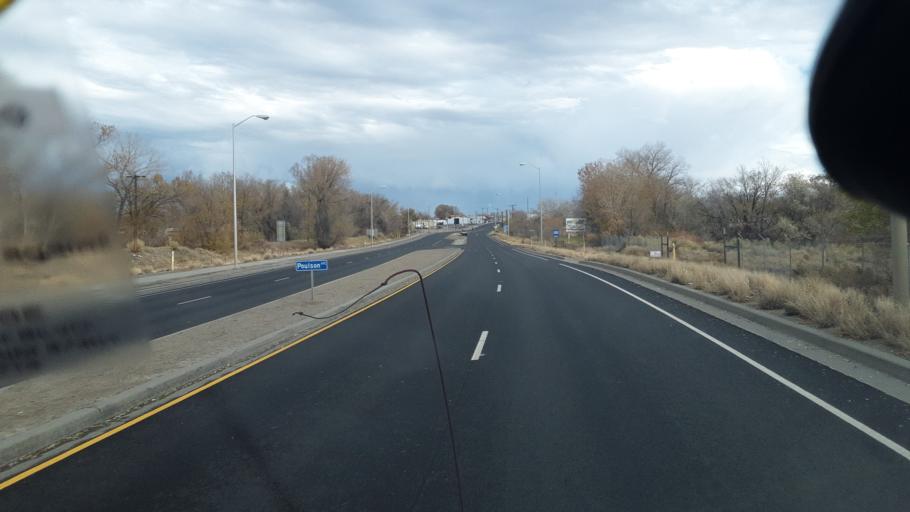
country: US
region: New Mexico
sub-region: San Juan County
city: Farmington
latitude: 36.7191
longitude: -108.2066
